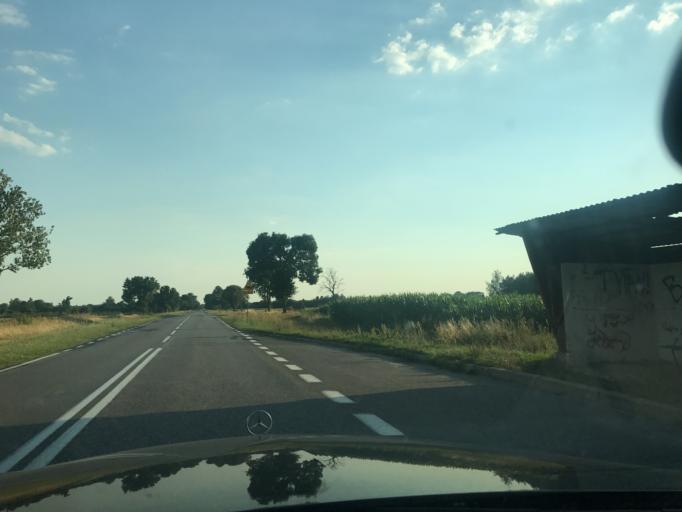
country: PL
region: Lublin Voivodeship
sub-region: Powiat bialski
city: Wisznice
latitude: 51.7642
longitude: 23.1875
